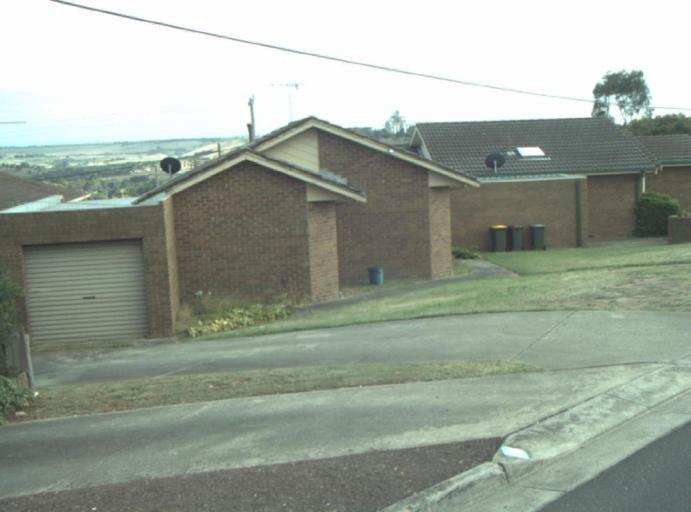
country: AU
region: Victoria
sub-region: Greater Geelong
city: Wandana Heights
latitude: -38.1537
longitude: 144.3115
